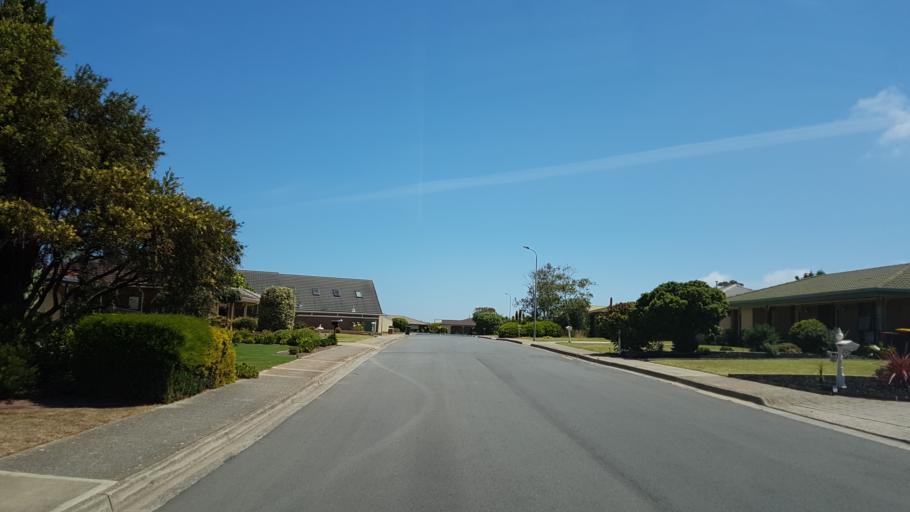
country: AU
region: South Australia
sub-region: Marion
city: Marino
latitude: -35.0645
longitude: 138.5153
